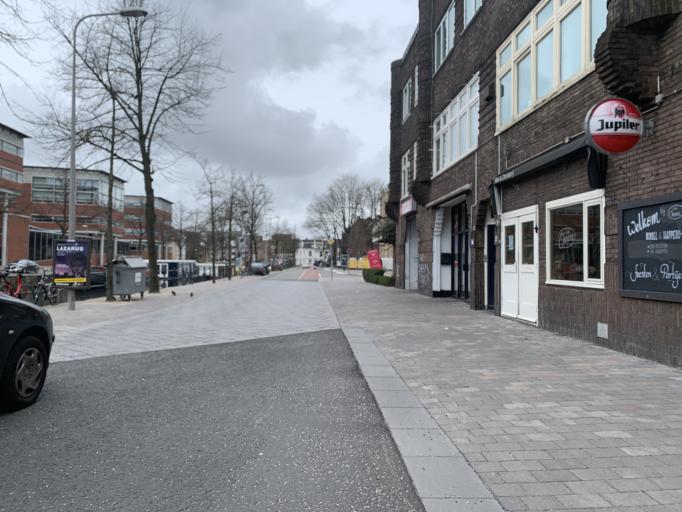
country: NL
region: Groningen
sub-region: Gemeente Groningen
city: Groningen
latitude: 53.2201
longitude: 6.5720
